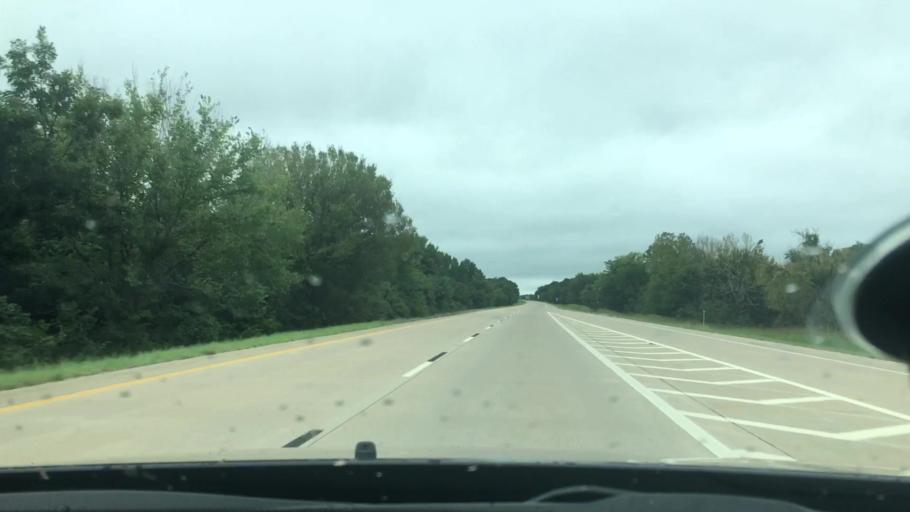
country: US
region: Oklahoma
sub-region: McIntosh County
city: Checotah
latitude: 35.4517
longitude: -95.7129
